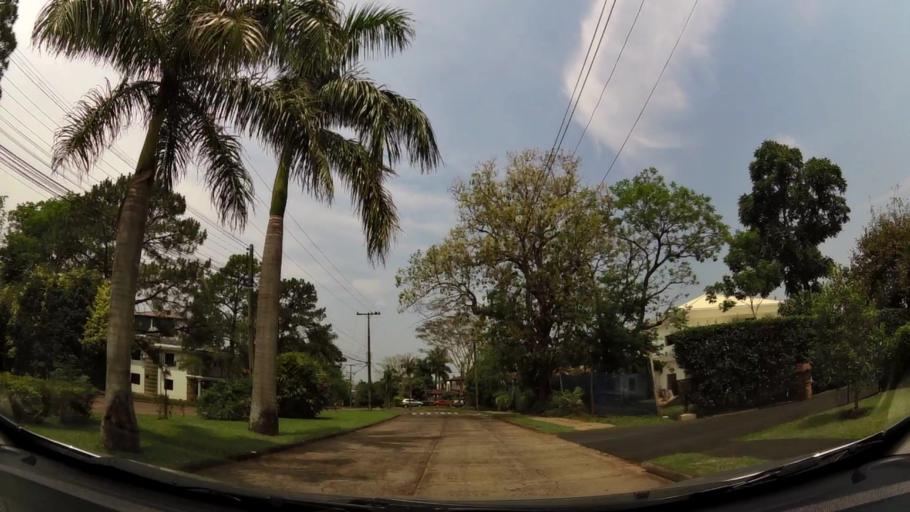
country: PY
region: Alto Parana
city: Ciudad del Este
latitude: -25.4953
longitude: -54.6110
